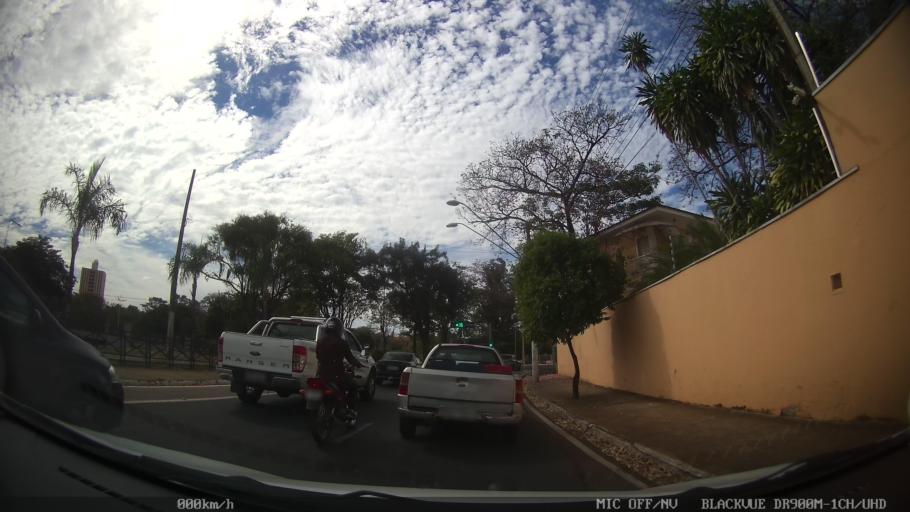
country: BR
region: Sao Paulo
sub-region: Catanduva
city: Catanduva
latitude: -21.1392
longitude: -48.9666
